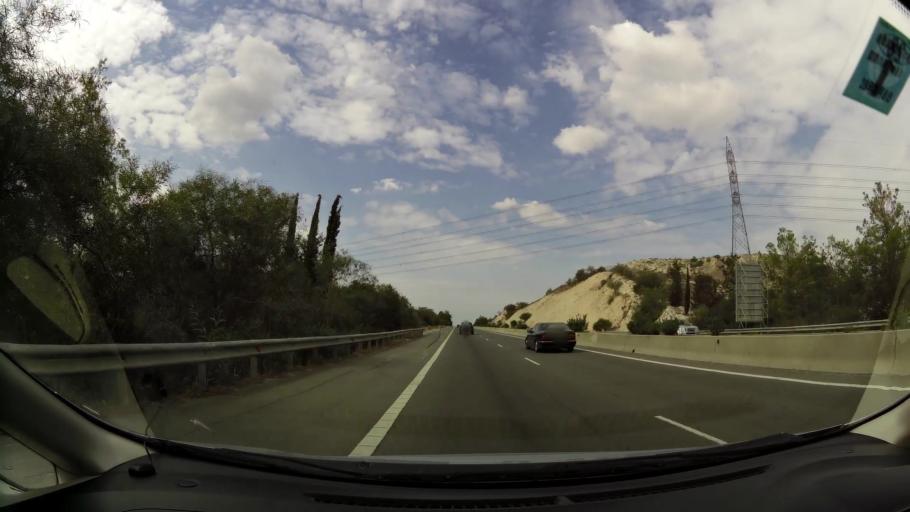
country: CY
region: Lefkosia
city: Dali
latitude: 34.9977
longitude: 33.4316
